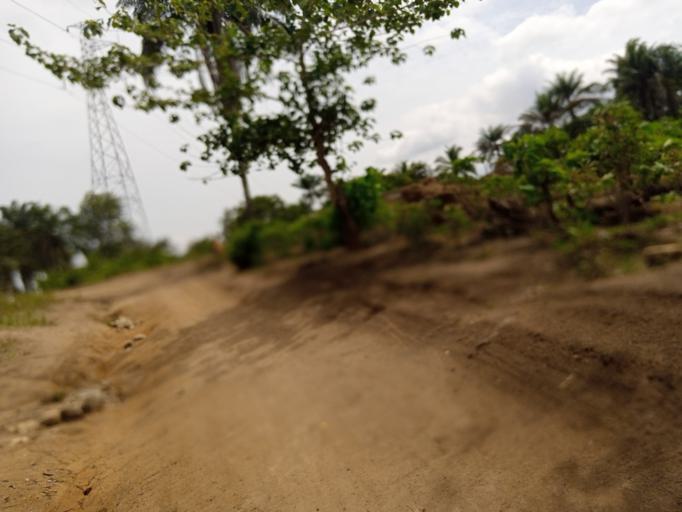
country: SL
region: Western Area
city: Waterloo
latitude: 8.3325
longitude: -13.0058
